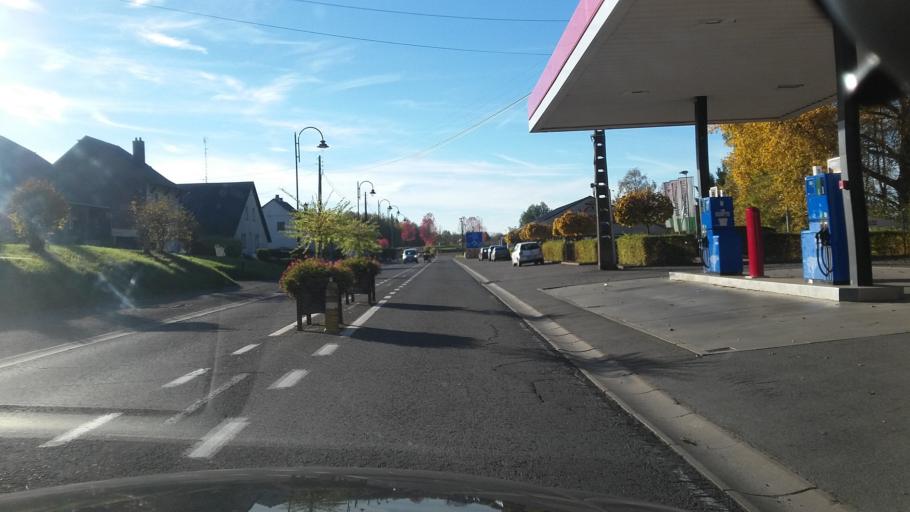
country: BE
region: Wallonia
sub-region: Province du Luxembourg
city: Etalle
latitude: 49.6732
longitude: 5.5946
